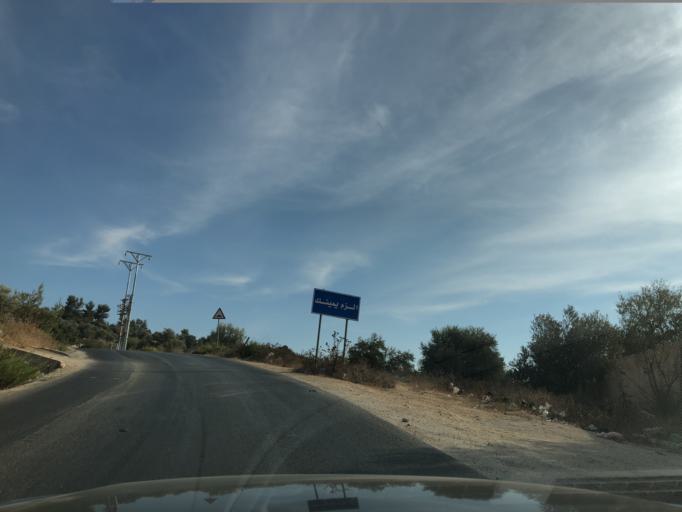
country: JO
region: Irbid
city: `Ayn Jannah
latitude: 32.3262
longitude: 35.7607
